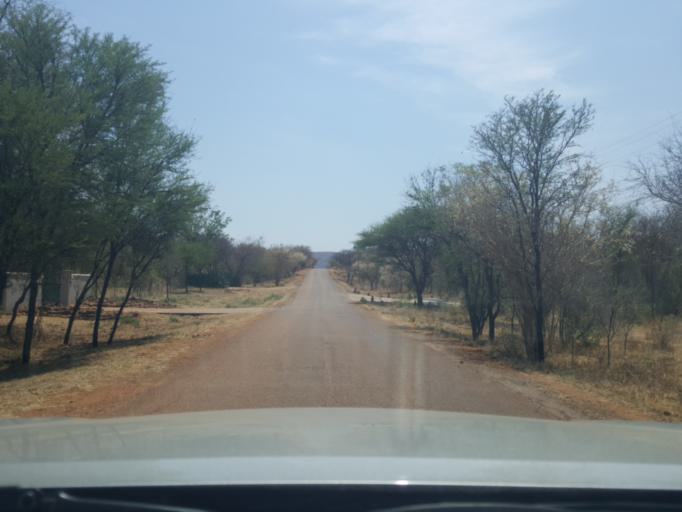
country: BW
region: South East
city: Ramotswa
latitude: -24.7695
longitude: 25.8452
